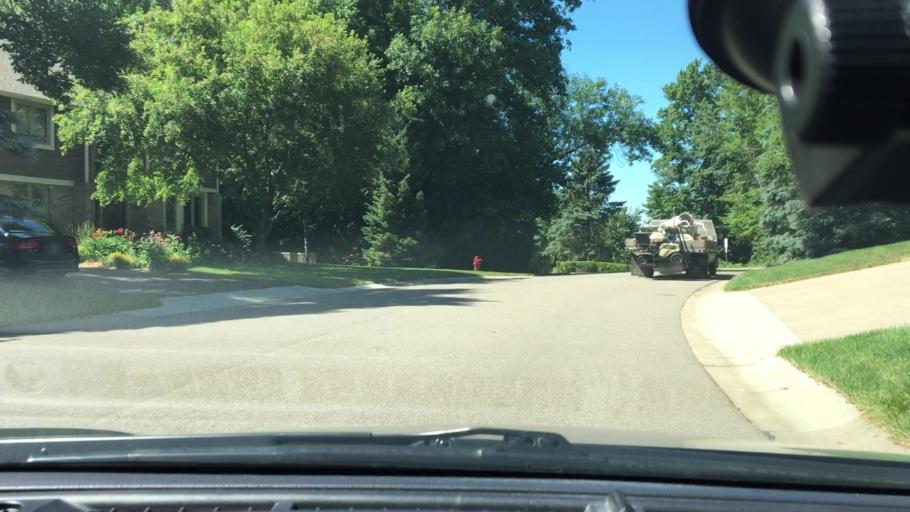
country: US
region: Minnesota
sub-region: Hennepin County
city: Maple Grove
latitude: 45.0691
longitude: -93.4621
